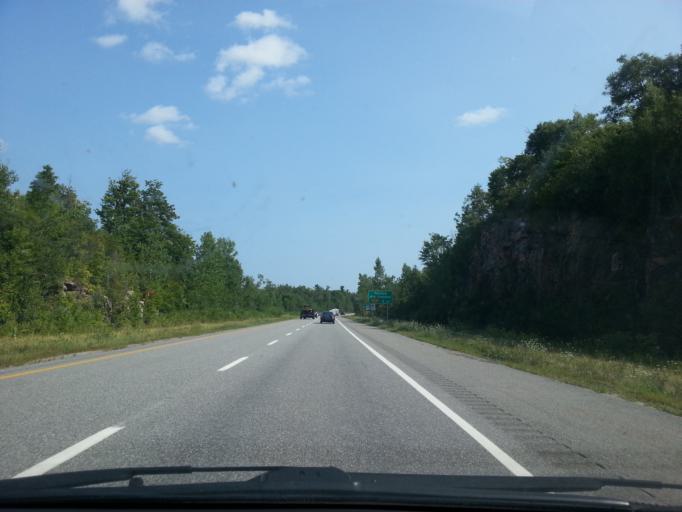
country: CA
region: Quebec
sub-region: Outaouais
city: Wakefield
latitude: 45.5311
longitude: -75.8268
